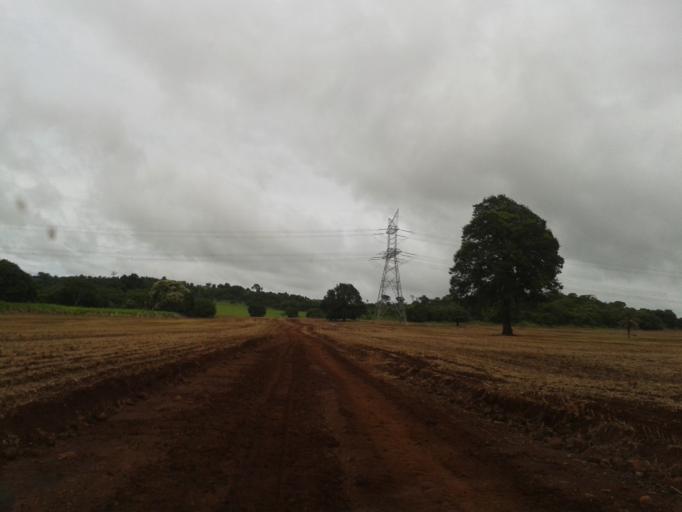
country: BR
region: Minas Gerais
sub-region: Capinopolis
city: Capinopolis
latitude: -18.7270
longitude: -49.7715
